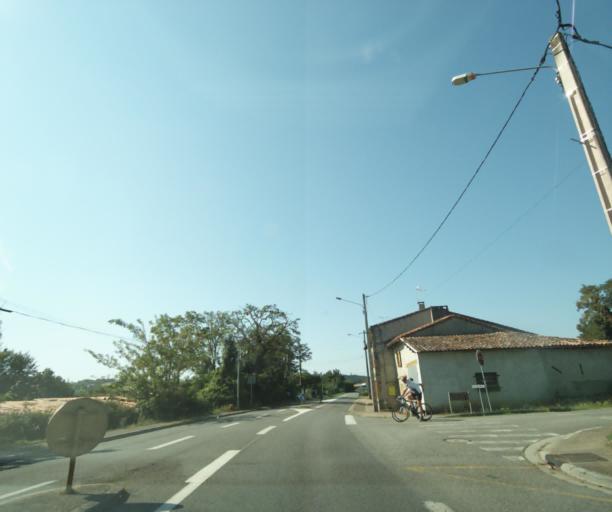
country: FR
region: Midi-Pyrenees
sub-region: Departement de la Haute-Garonne
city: Beaumont-sur-Leze
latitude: 43.3855
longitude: 1.3478
